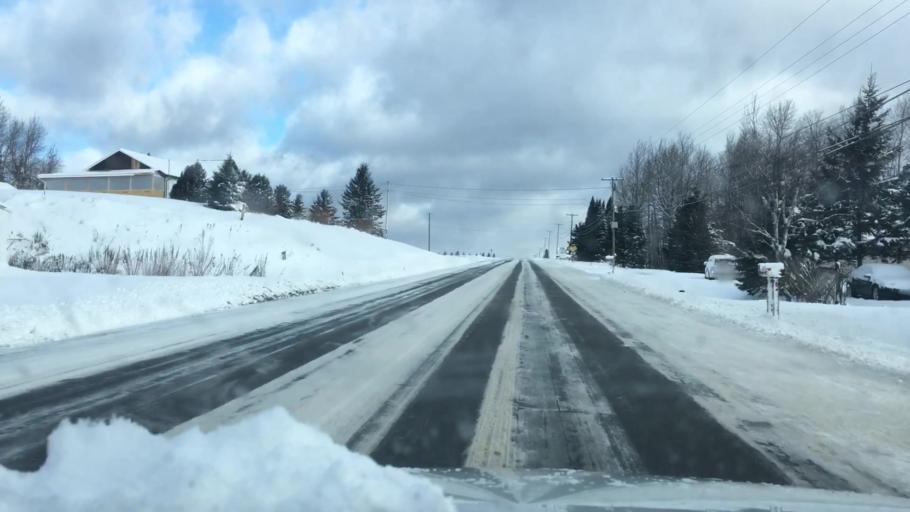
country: US
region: Maine
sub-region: Aroostook County
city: Caribou
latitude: 46.9337
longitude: -68.0234
